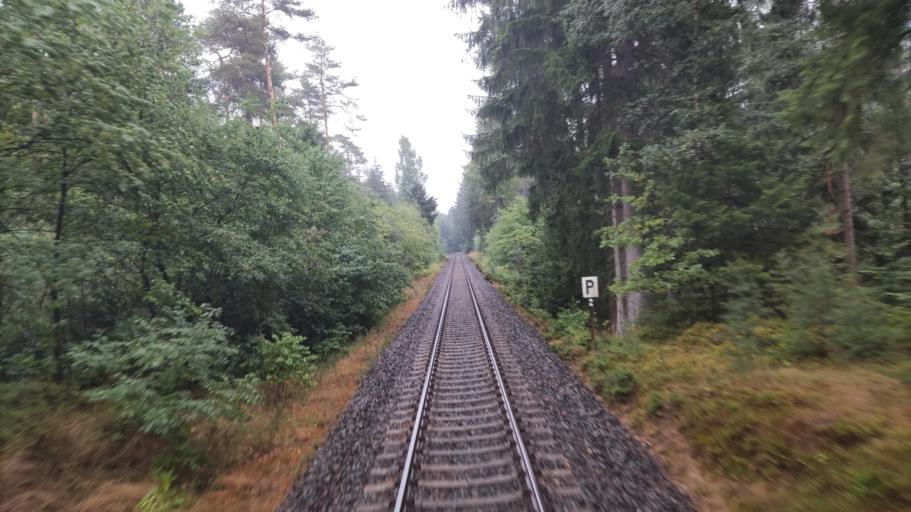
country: DE
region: Lower Saxony
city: Bispingen
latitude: 53.0642
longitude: 9.9720
